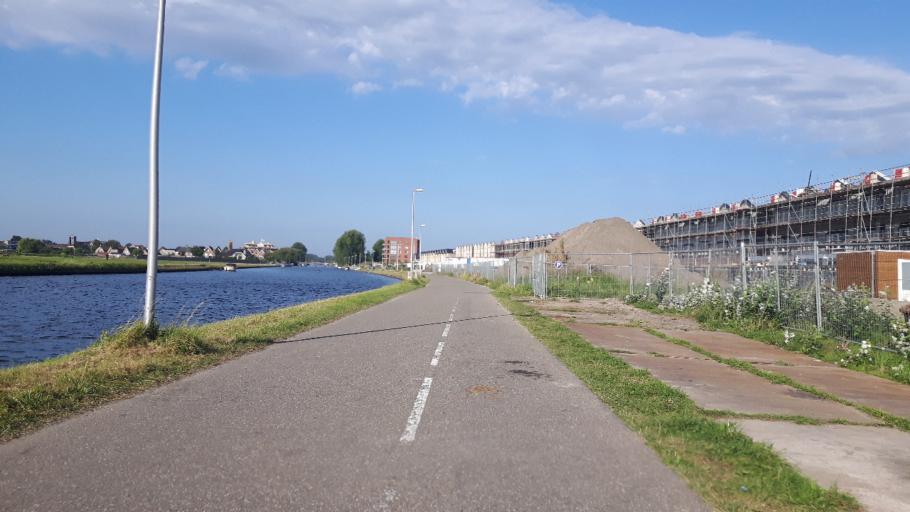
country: NL
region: South Holland
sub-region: Gemeente Katwijk
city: Rijnsburg
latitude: 52.1953
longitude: 4.4547
